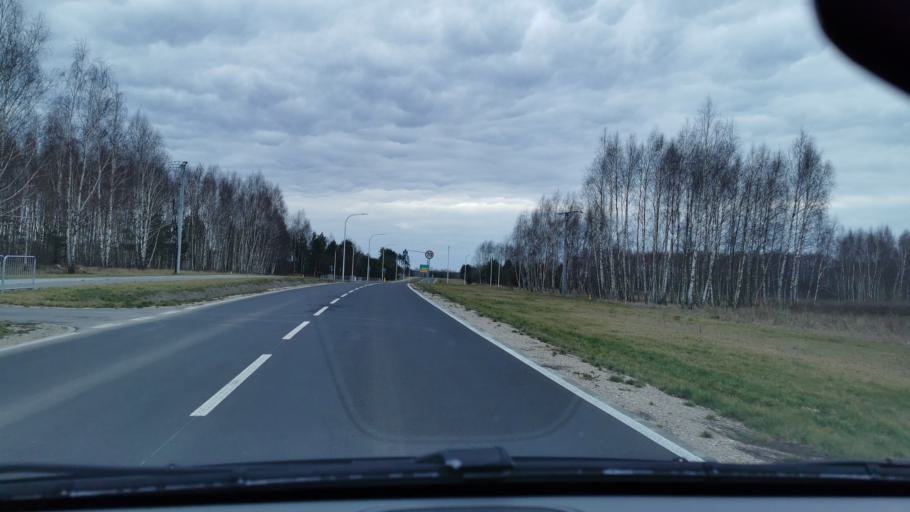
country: PL
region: Masovian Voivodeship
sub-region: Powiat zyrardowski
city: Zyrardow
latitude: 52.0041
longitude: 20.4645
